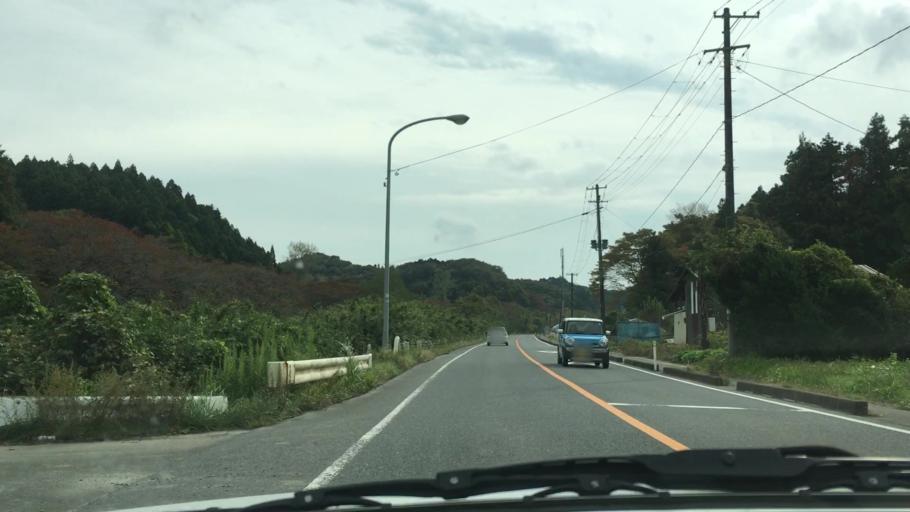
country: JP
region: Miyagi
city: Matsushima
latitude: 38.4292
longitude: 141.0605
